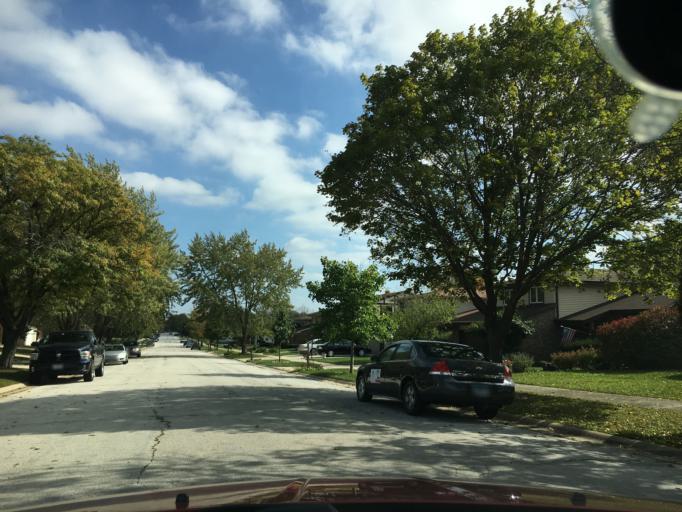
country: US
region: Illinois
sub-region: Cook County
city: Tinley Park
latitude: 41.6077
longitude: -87.7821
